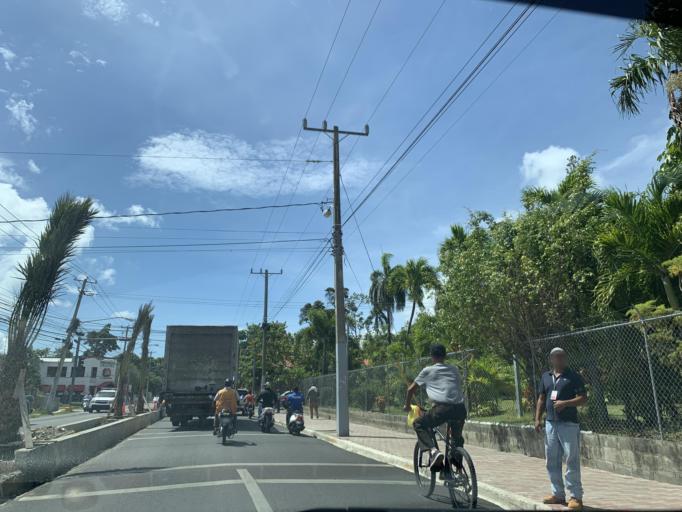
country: DO
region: Puerto Plata
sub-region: Puerto Plata
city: Puerto Plata
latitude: 19.7911
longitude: -70.6810
